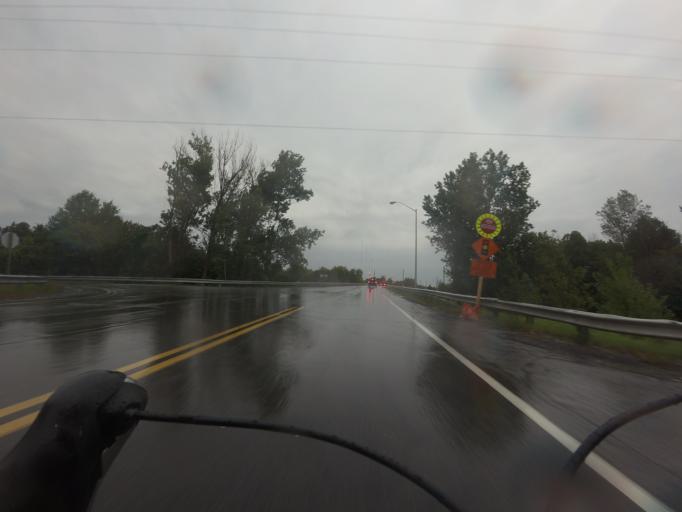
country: CA
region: Ontario
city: Bells Corners
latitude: 45.1920
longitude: -75.7251
